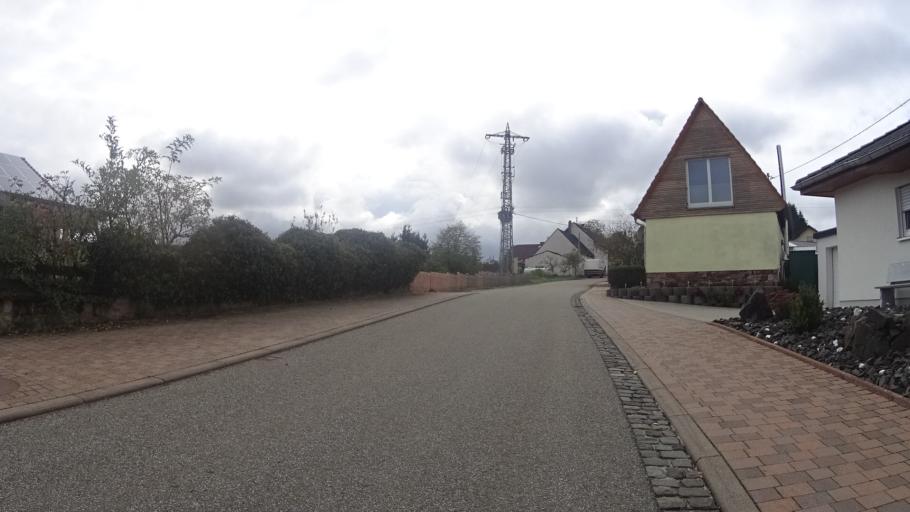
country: DE
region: Rheinland-Pfalz
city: Ruppertsecken
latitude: 49.6503
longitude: 7.9025
